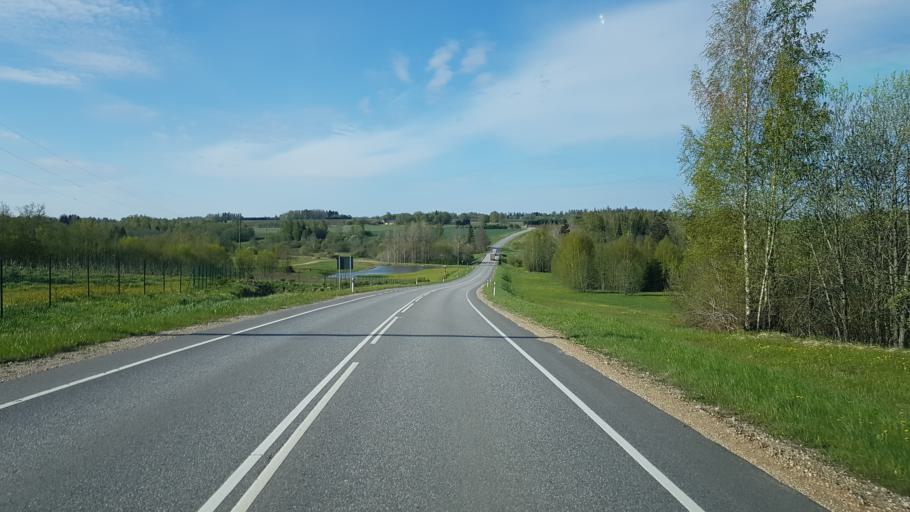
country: EE
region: Viljandimaa
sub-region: Karksi vald
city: Karksi-Nuia
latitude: 58.1507
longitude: 25.5963
